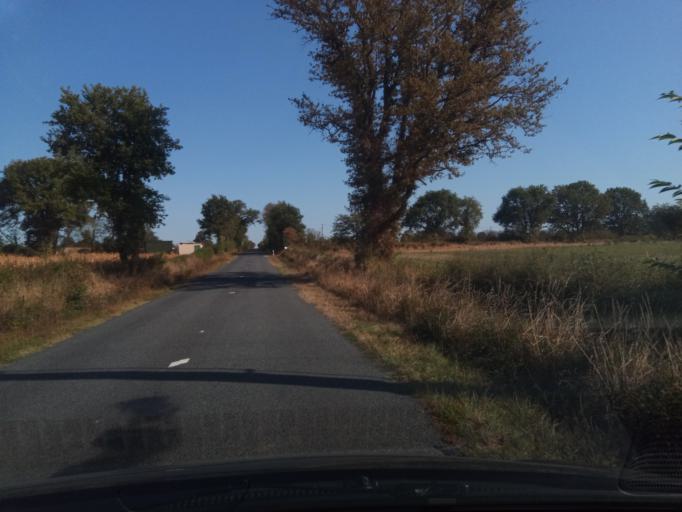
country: FR
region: Poitou-Charentes
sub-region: Departement de la Vienne
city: Saulge
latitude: 46.3532
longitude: 0.8726
